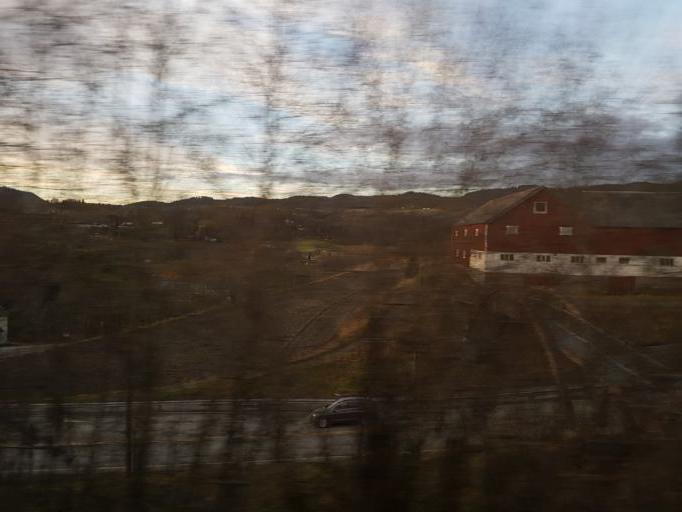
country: NO
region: Sor-Trondelag
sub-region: Melhus
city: Lundamo
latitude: 63.2169
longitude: 10.2956
